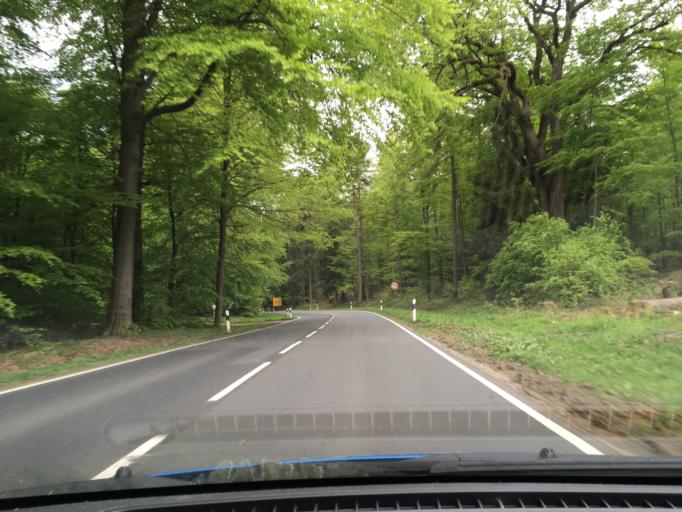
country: DE
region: Lower Saxony
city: Derental
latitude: 51.6847
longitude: 9.4511
